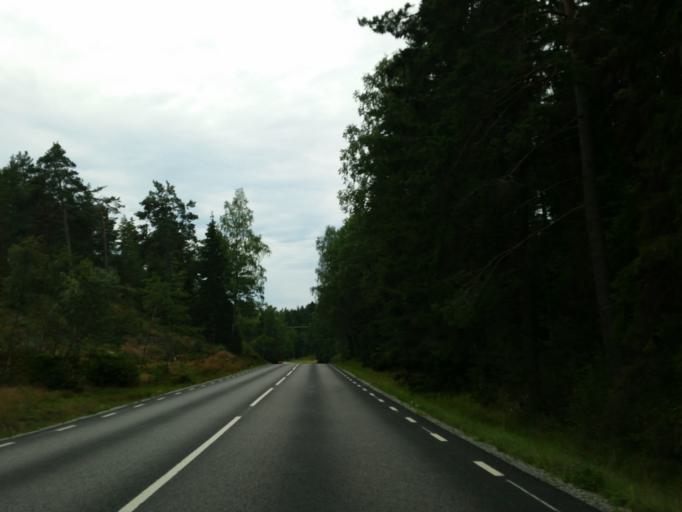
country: SE
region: Stockholm
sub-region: Salems Kommun
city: Ronninge
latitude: 59.2282
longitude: 17.6866
